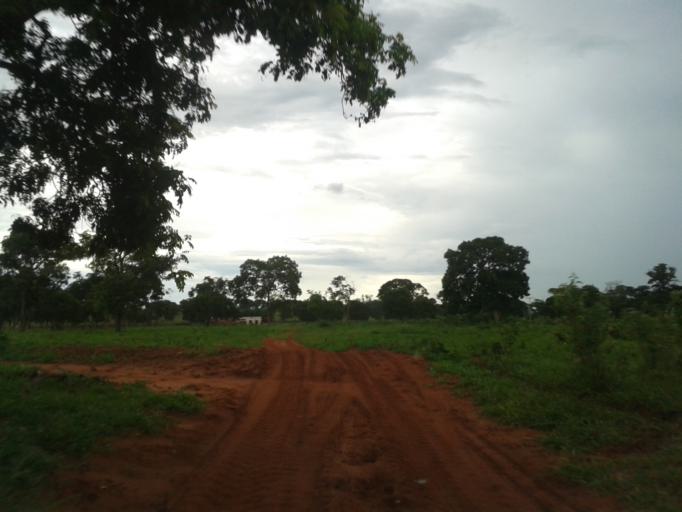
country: BR
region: Minas Gerais
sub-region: Santa Vitoria
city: Santa Vitoria
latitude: -19.1994
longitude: -50.5151
